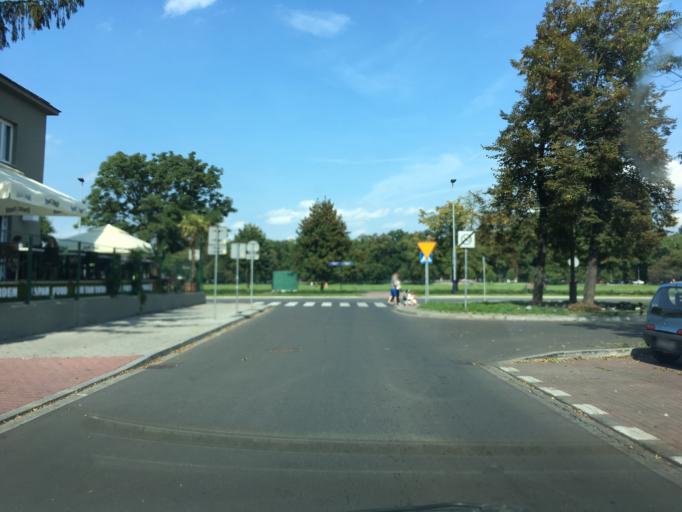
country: PL
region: Lesser Poland Voivodeship
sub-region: Krakow
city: Krakow
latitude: 50.0577
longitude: 19.9178
